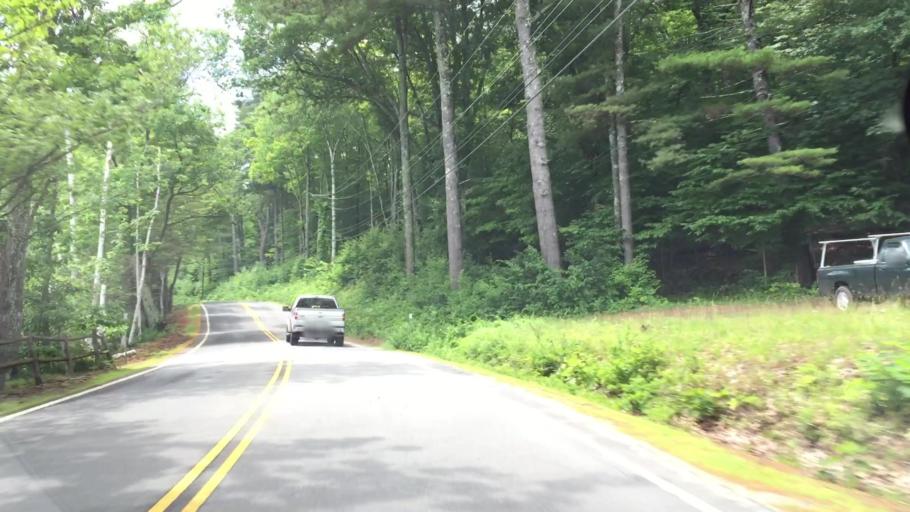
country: US
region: New Hampshire
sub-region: Grafton County
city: Holderness
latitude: 43.7642
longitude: -71.5591
